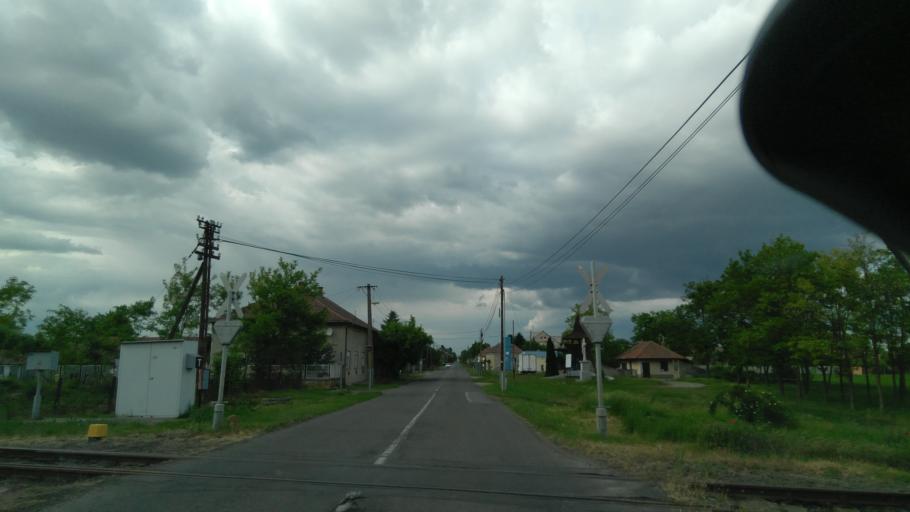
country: HU
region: Bekes
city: Gadoros
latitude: 46.6562
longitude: 20.5901
